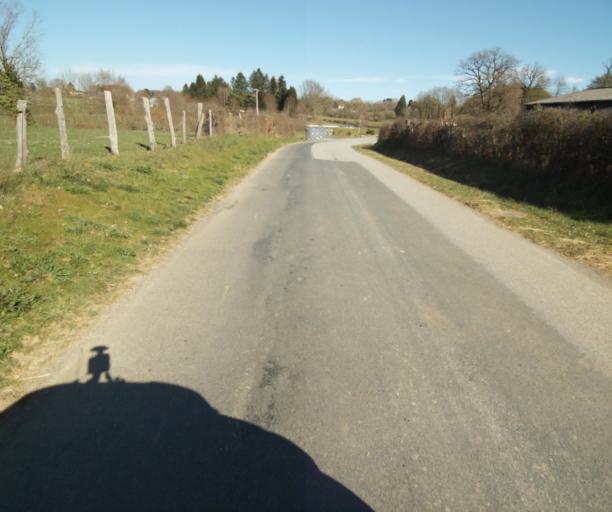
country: FR
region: Limousin
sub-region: Departement de la Correze
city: Chamboulive
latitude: 45.4684
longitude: 1.7279
